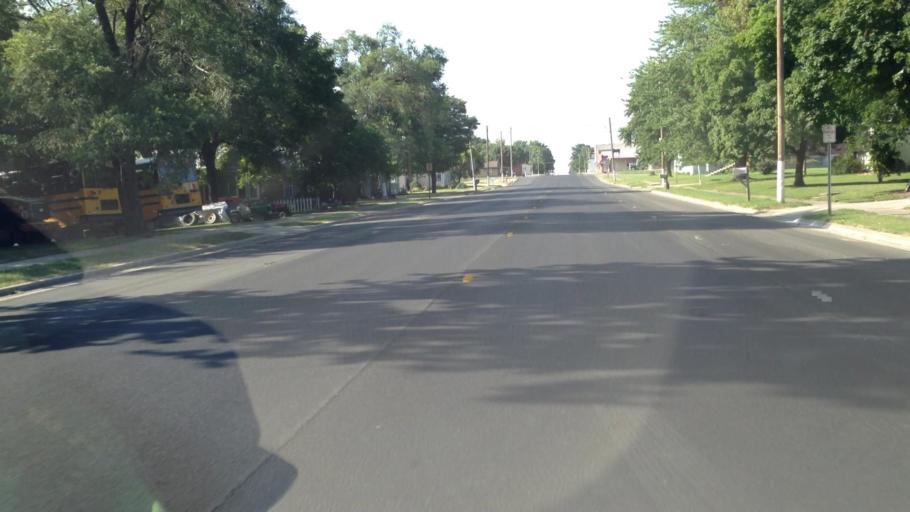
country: US
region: Kansas
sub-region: Allen County
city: Iola
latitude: 37.9124
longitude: -95.1701
